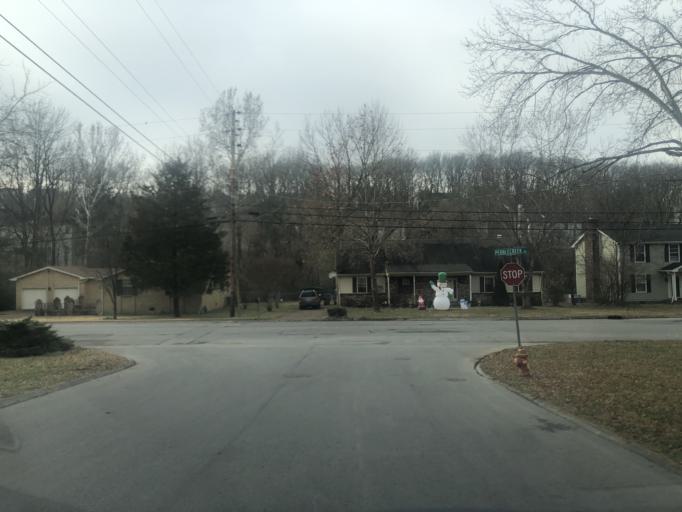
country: US
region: Tennessee
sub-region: Rutherford County
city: La Vergne
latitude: 36.0727
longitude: -86.6586
